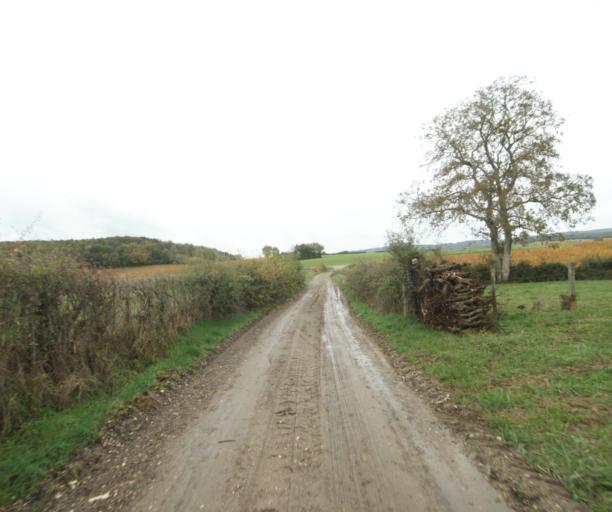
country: FR
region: Bourgogne
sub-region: Departement de Saone-et-Loire
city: Saint-Martin-Belle-Roche
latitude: 46.4718
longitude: 4.8511
